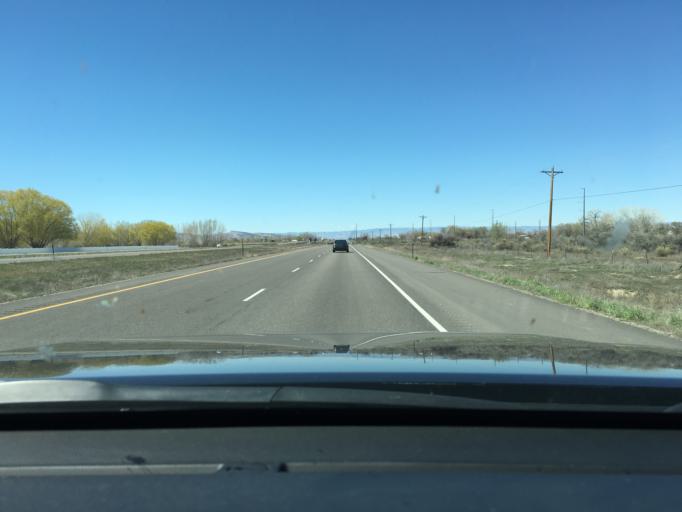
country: US
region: Colorado
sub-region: Mesa County
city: Fruita
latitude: 39.1339
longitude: -108.6934
